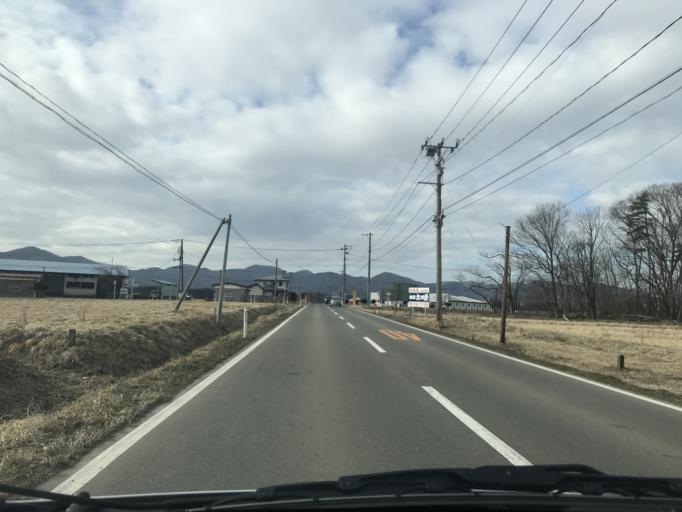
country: JP
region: Iwate
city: Hanamaki
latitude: 39.4137
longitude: 141.0938
